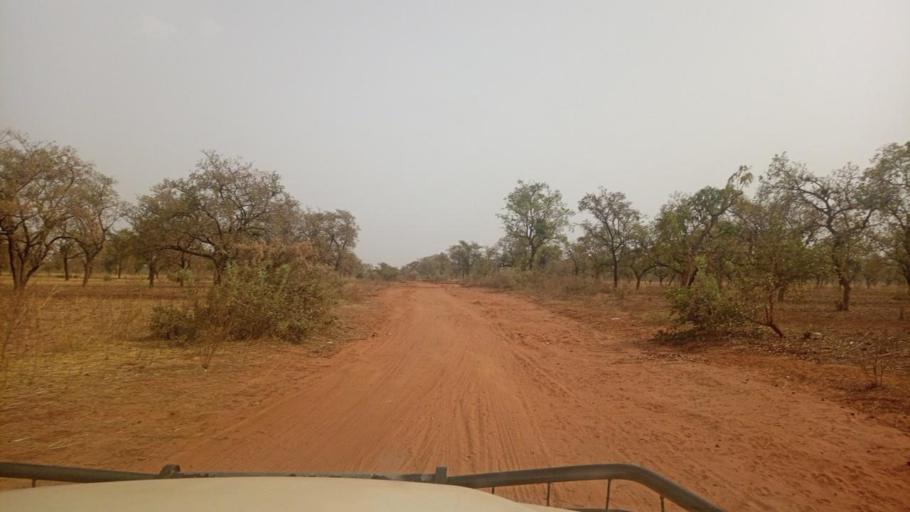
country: BF
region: Boucle du Mouhoun
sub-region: Province des Banwa
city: Salanso
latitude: 12.1051
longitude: -4.3349
